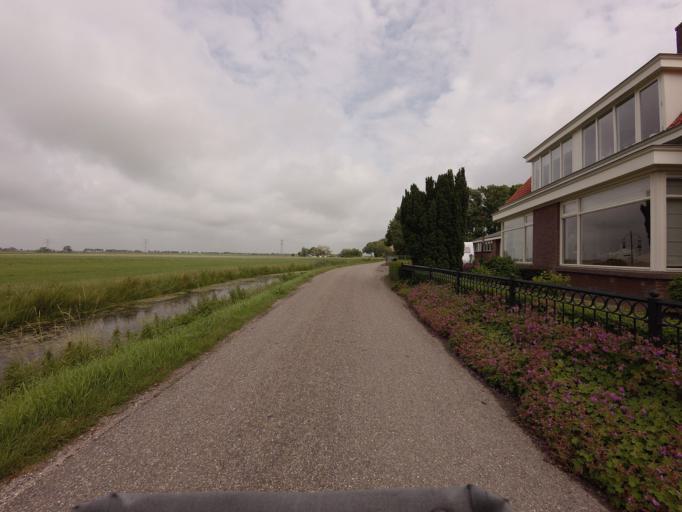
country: NL
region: North Holland
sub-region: Gemeente Schagen
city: Schagen
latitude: 52.7934
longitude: 4.8202
